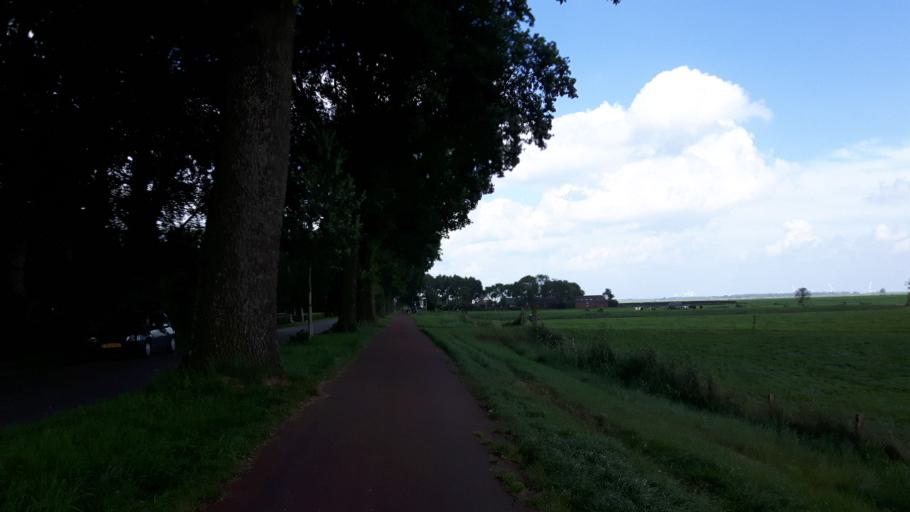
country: NL
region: North Holland
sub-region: Gemeente Blaricum
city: Blaricum
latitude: 52.2570
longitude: 5.2690
